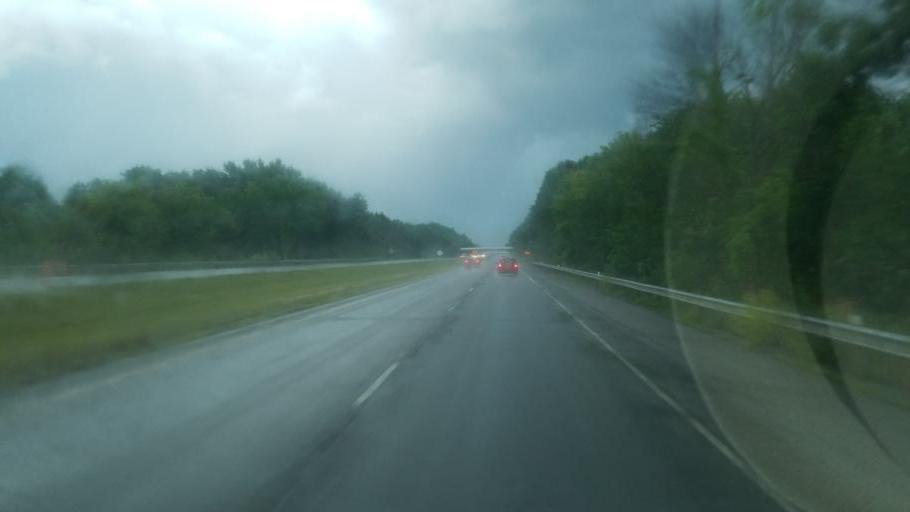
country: US
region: Ohio
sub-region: Summit County
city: Norton
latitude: 41.0597
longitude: -81.6623
